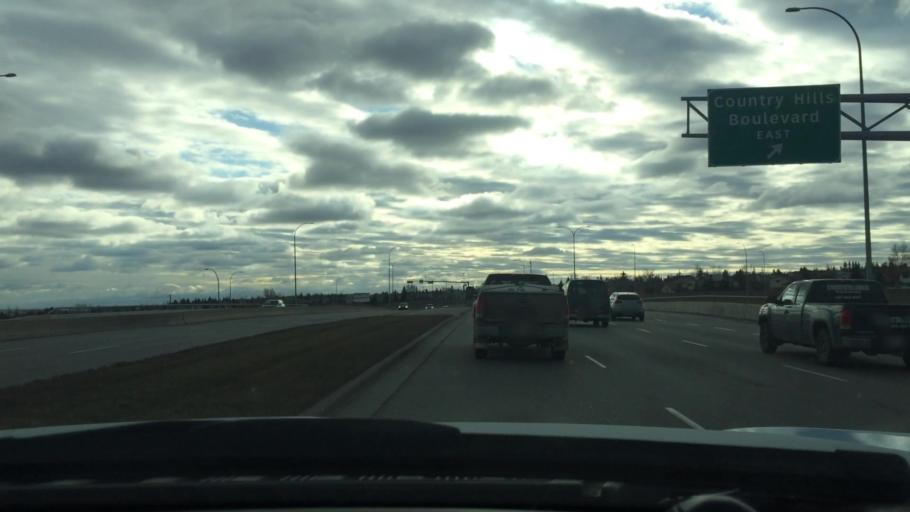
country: CA
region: Alberta
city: Calgary
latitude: 51.1446
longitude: -114.0933
